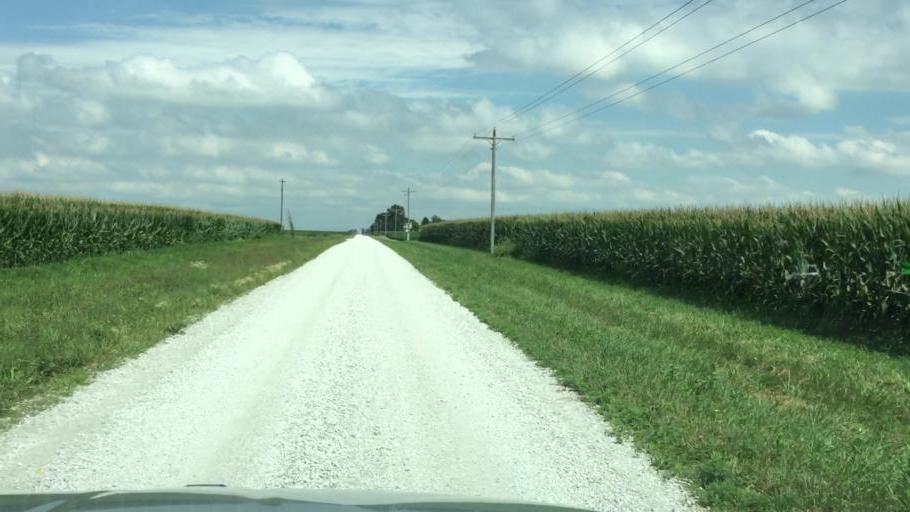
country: US
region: Illinois
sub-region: Hancock County
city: Nauvoo
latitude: 40.5218
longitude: -91.2997
